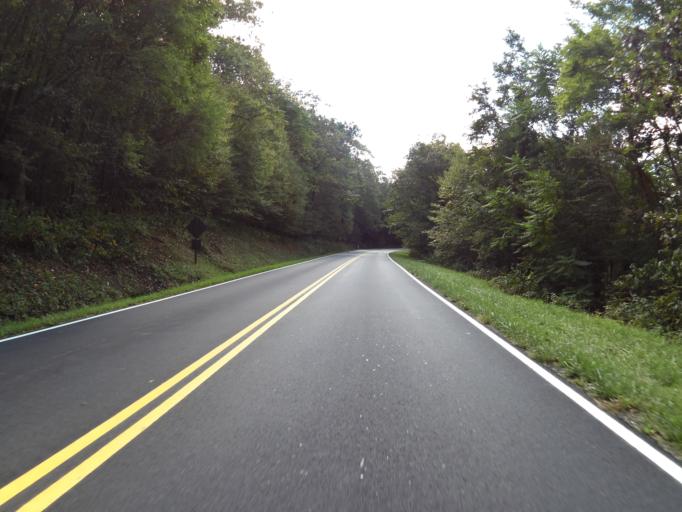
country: US
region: Virginia
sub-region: Rappahannock County
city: Washington
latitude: 38.7533
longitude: -78.3035
